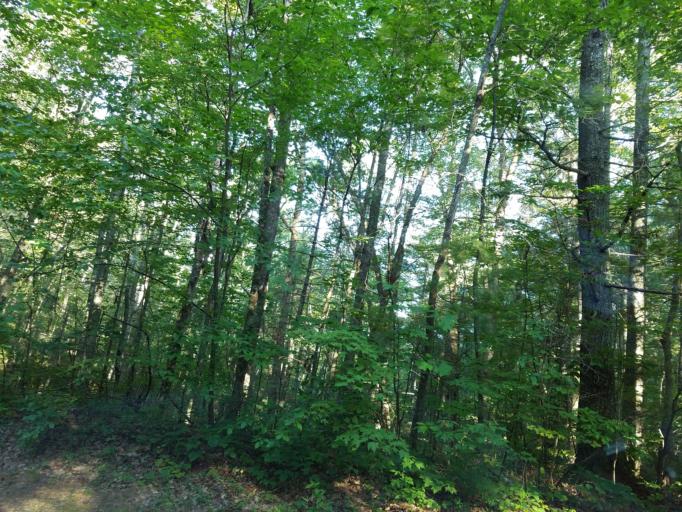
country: US
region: Georgia
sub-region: Fannin County
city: Blue Ridge
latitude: 34.8018
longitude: -84.1737
